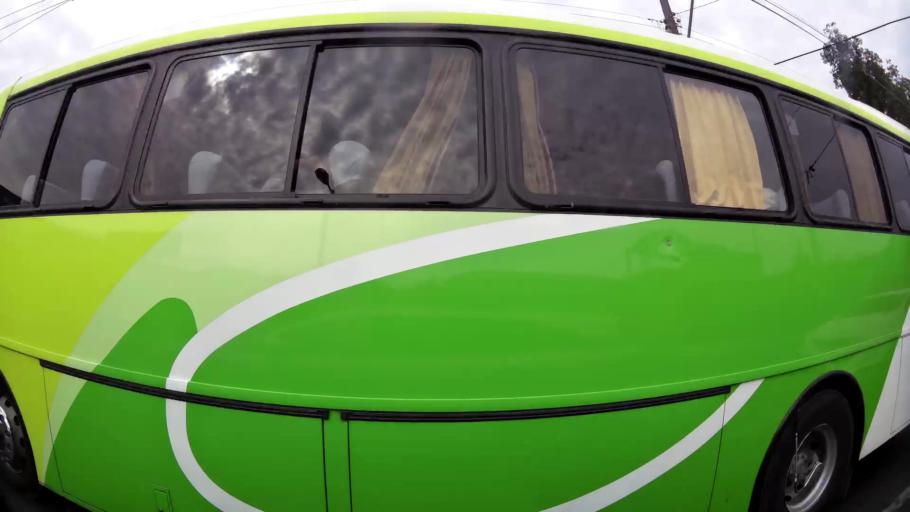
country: CL
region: Santiago Metropolitan
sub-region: Provincia de Santiago
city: Lo Prado
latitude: -33.5174
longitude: -70.7556
